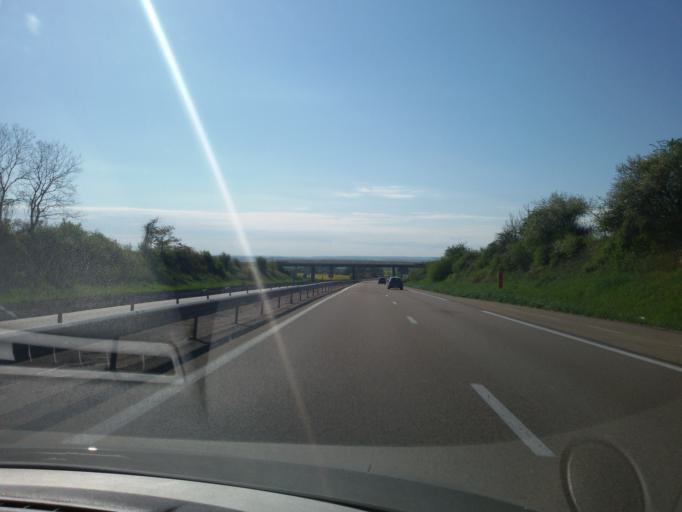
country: FR
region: Bourgogne
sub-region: Departement de l'Yonne
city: Vermenton
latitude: 47.7349
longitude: 3.7369
